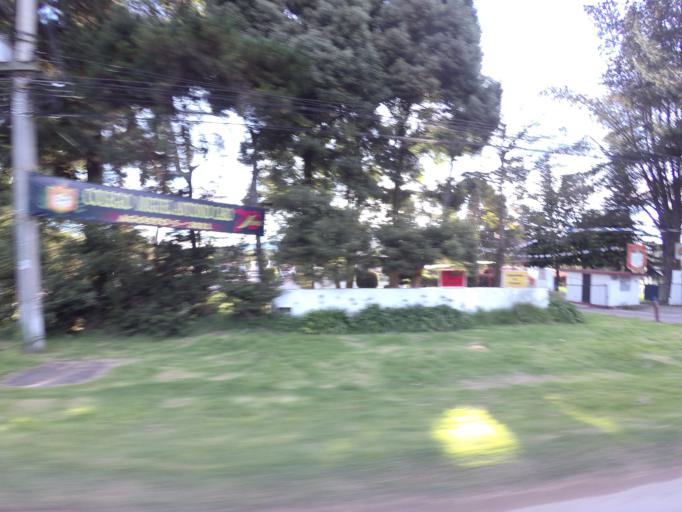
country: CO
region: Cundinamarca
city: Chia
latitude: 4.8129
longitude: -74.0310
